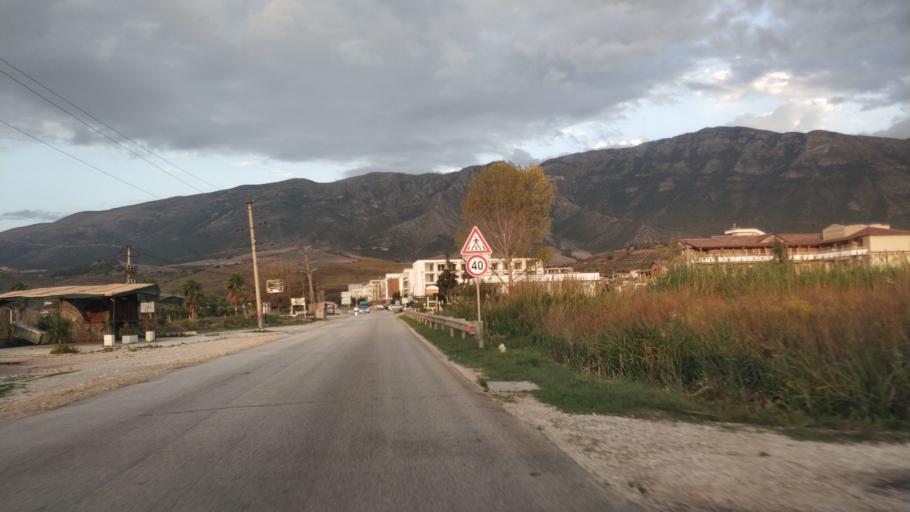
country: AL
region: Vlore
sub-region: Rrethi i Vlores
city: Orikum
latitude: 40.3409
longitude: 19.4778
